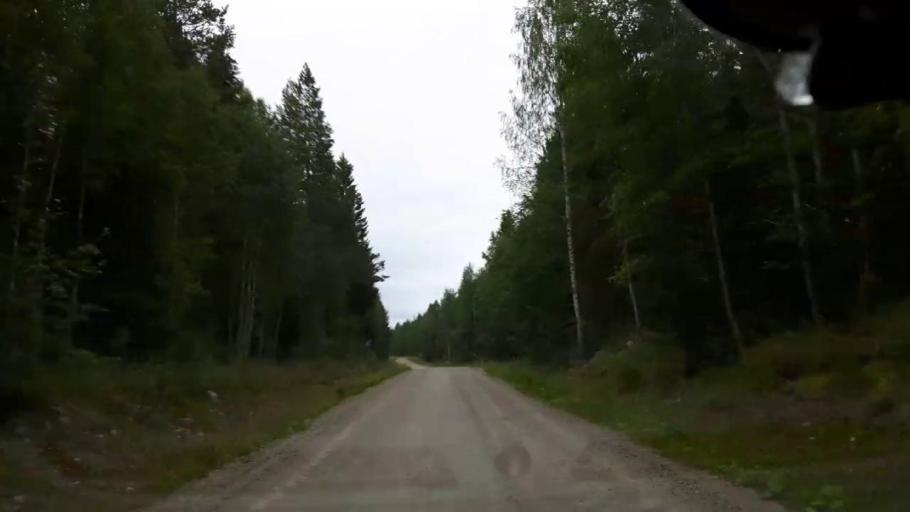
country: SE
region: Jaemtland
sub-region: Braecke Kommun
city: Braecke
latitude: 62.8242
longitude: 15.7116
